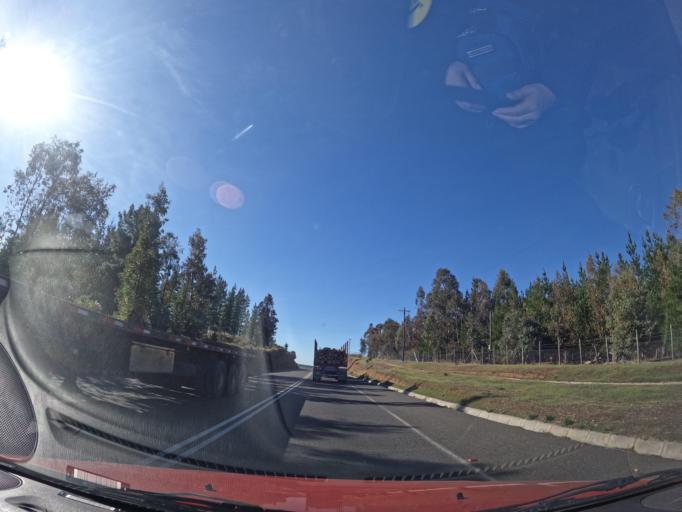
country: CL
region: Maule
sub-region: Provincia de Cauquenes
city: Cauquenes
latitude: -35.9294
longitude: -72.1865
